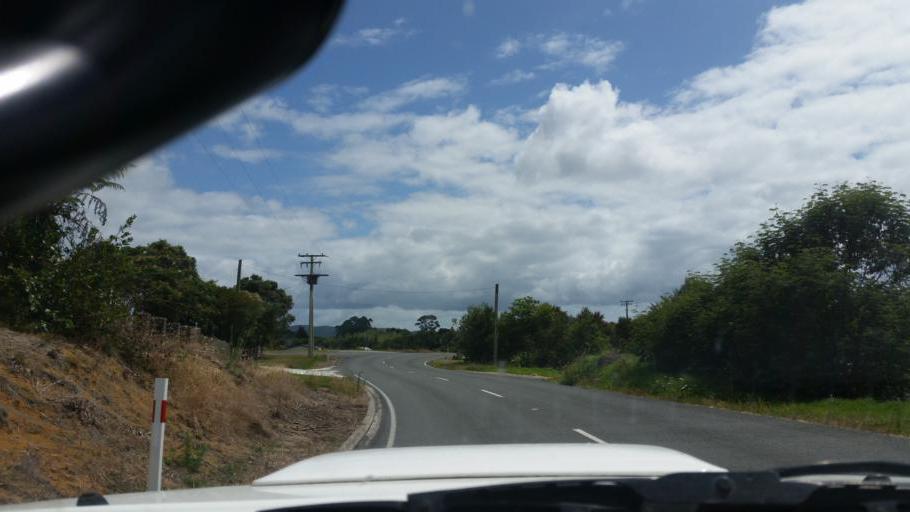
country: NZ
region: Auckland
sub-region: Auckland
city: Wellsford
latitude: -36.1391
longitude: 174.5574
